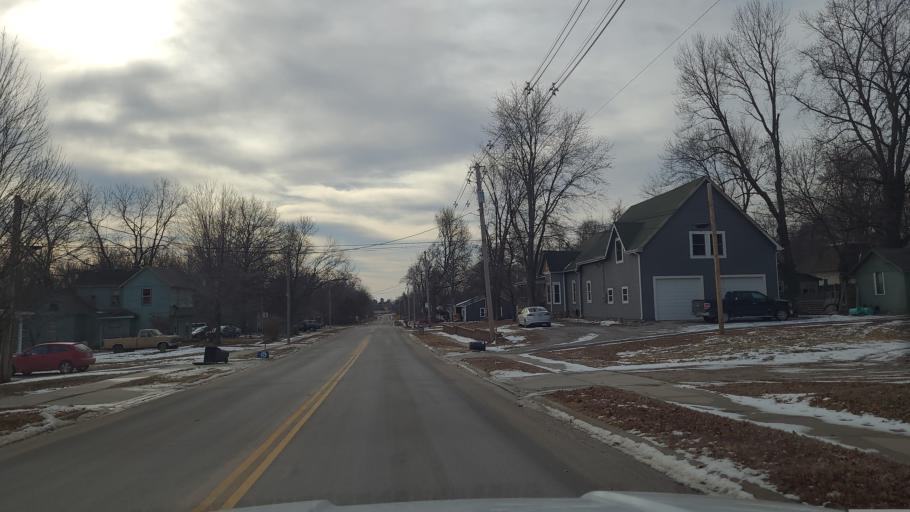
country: US
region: Kansas
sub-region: Douglas County
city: Baldwin City
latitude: 38.7737
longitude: -95.1862
